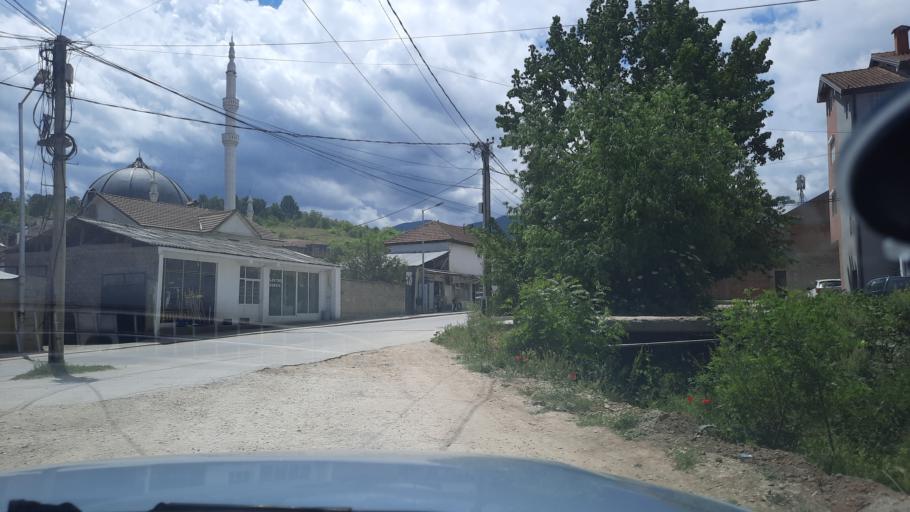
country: MK
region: Studenicani
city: Studenichani
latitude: 41.9212
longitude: 21.5354
